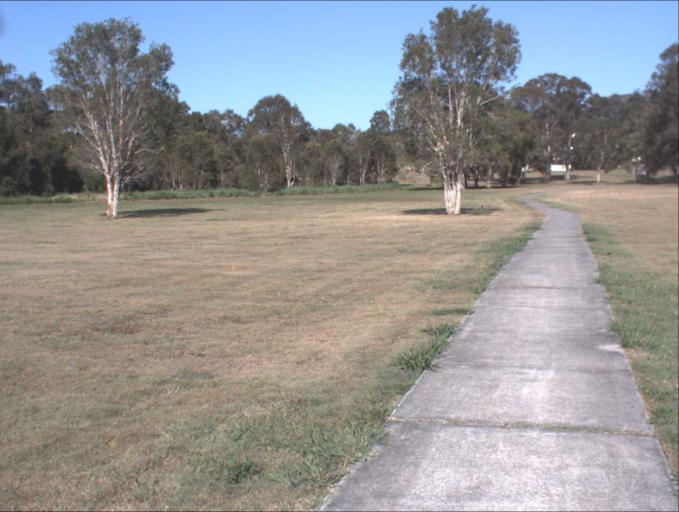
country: AU
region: Queensland
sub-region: Logan
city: Beenleigh
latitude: -27.6911
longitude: 153.2084
